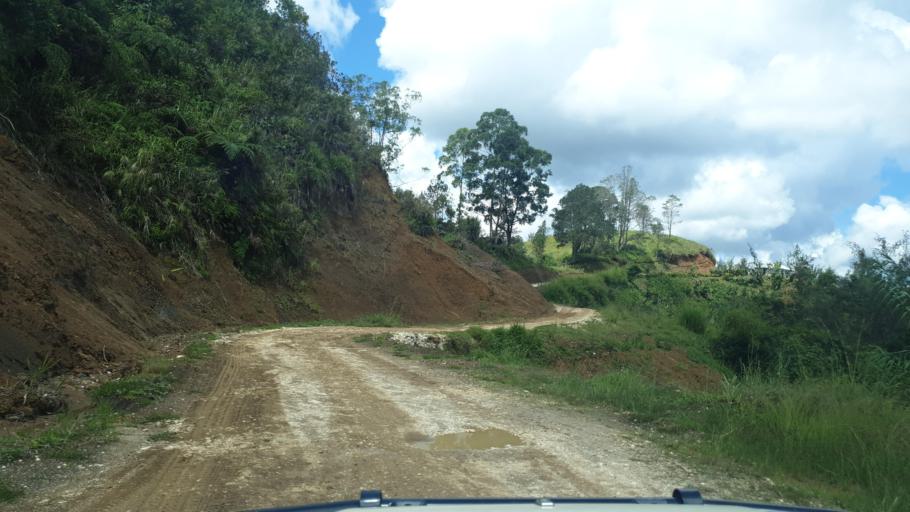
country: PG
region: Chimbu
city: Kundiawa
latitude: -6.2135
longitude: 145.1376
